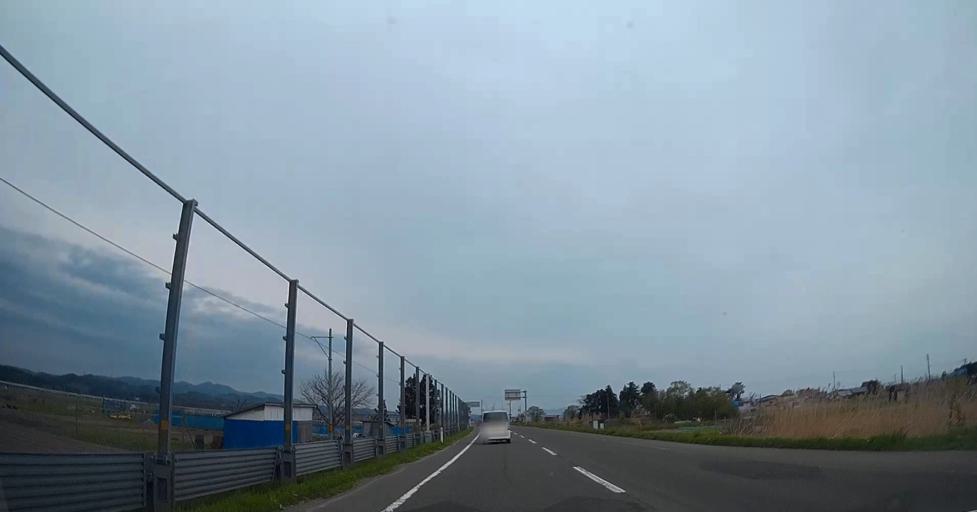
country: JP
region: Aomori
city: Aomori Shi
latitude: 40.9020
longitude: 140.6661
